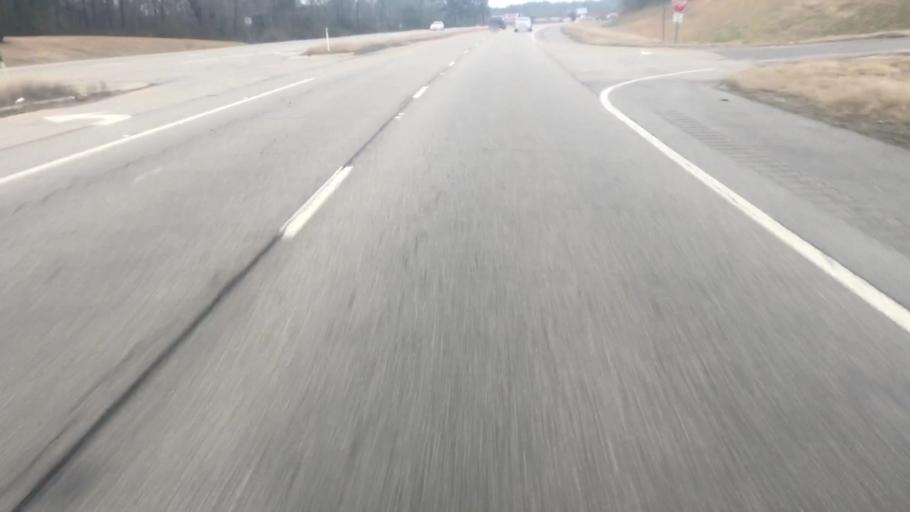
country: US
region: Alabama
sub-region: Walker County
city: Cordova
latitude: 33.8213
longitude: -87.1586
